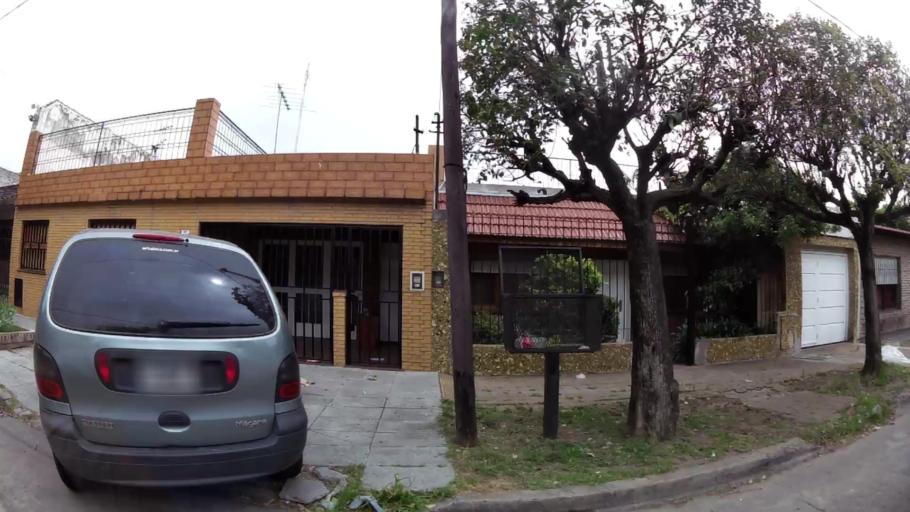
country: AR
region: Buenos Aires
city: San Justo
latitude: -34.6684
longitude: -58.5176
